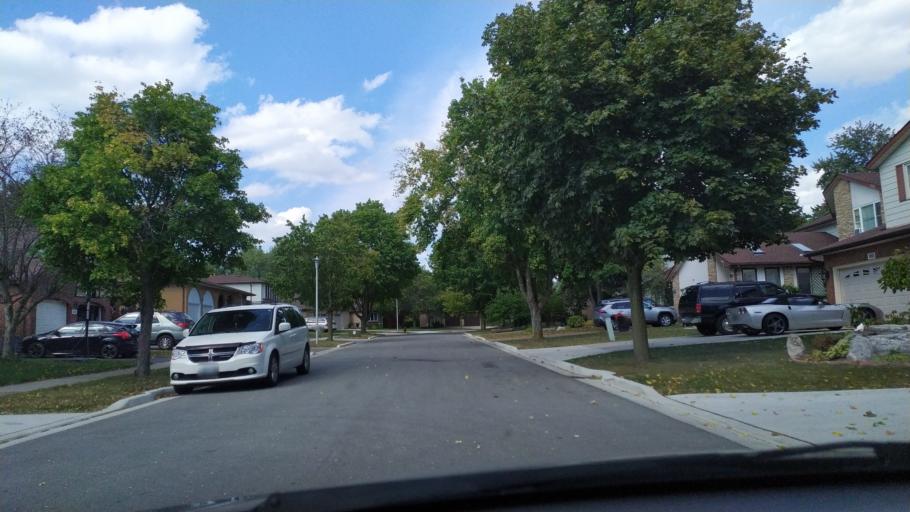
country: CA
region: Ontario
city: London
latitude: 42.9474
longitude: -81.2426
